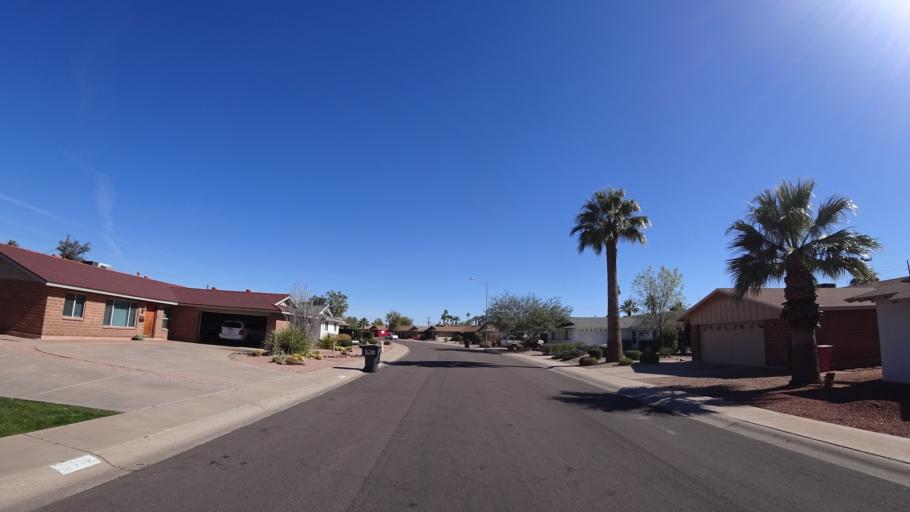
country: US
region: Arizona
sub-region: Maricopa County
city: Scottsdale
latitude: 33.5145
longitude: -111.8951
